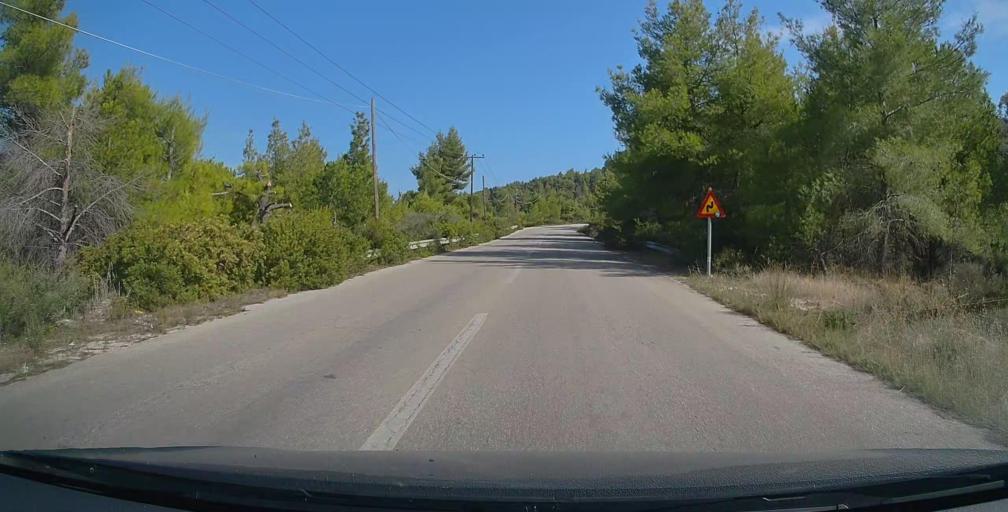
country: GR
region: Central Macedonia
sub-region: Nomos Chalkidikis
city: Sarti
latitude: 40.1164
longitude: 23.9767
